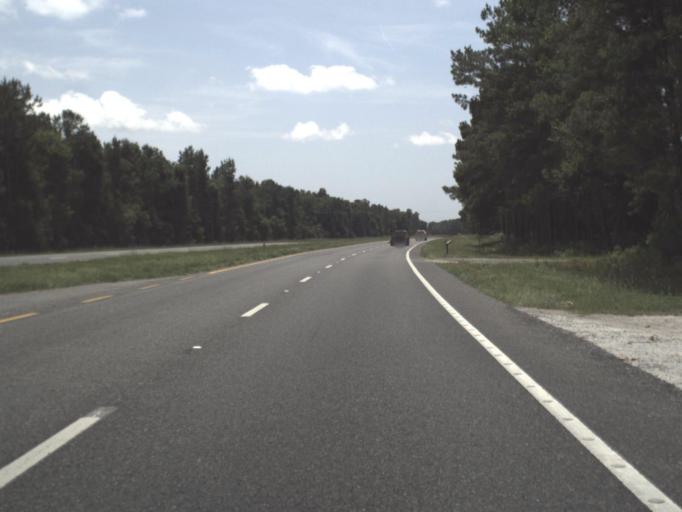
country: US
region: Florida
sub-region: Taylor County
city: Perry
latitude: 29.9934
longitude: -83.5008
